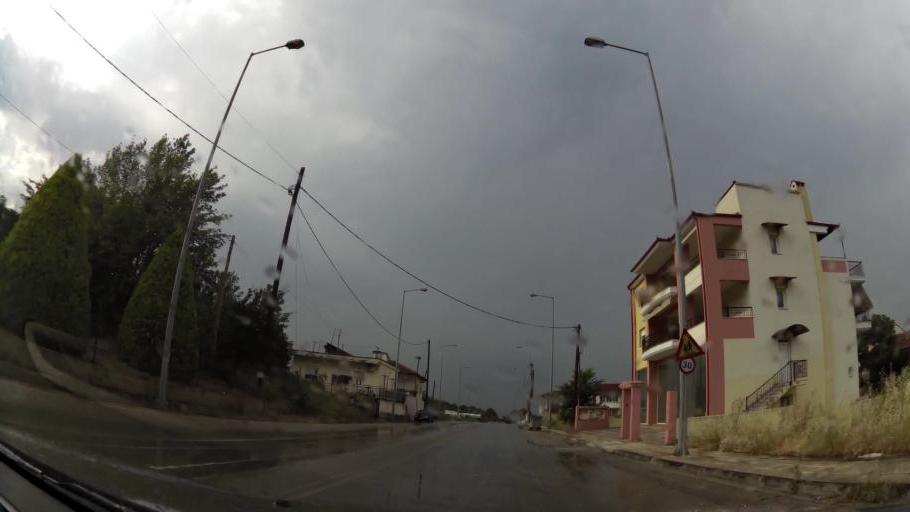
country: GR
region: Central Macedonia
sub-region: Nomos Imathias
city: Veroia
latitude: 40.5405
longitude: 22.1965
